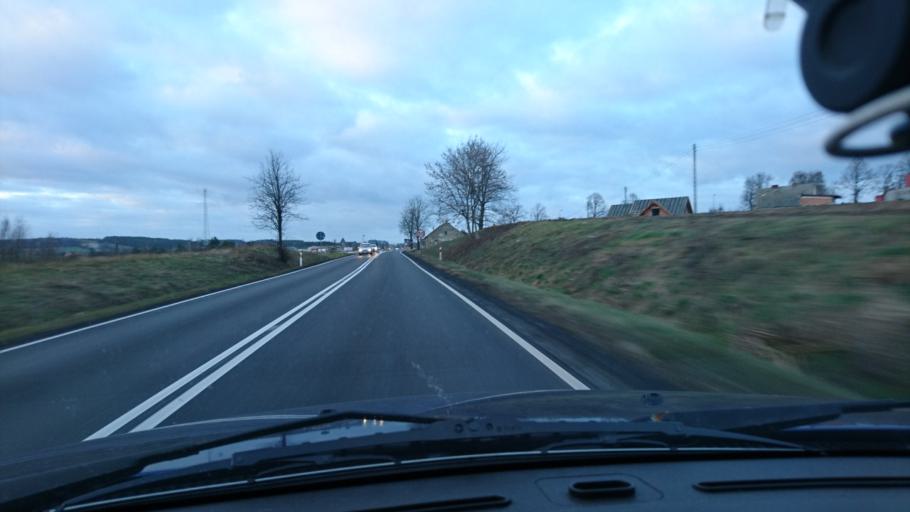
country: PL
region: Greater Poland Voivodeship
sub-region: Powiat ostrzeszowski
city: Ostrzeszow
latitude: 51.3855
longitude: 17.9493
